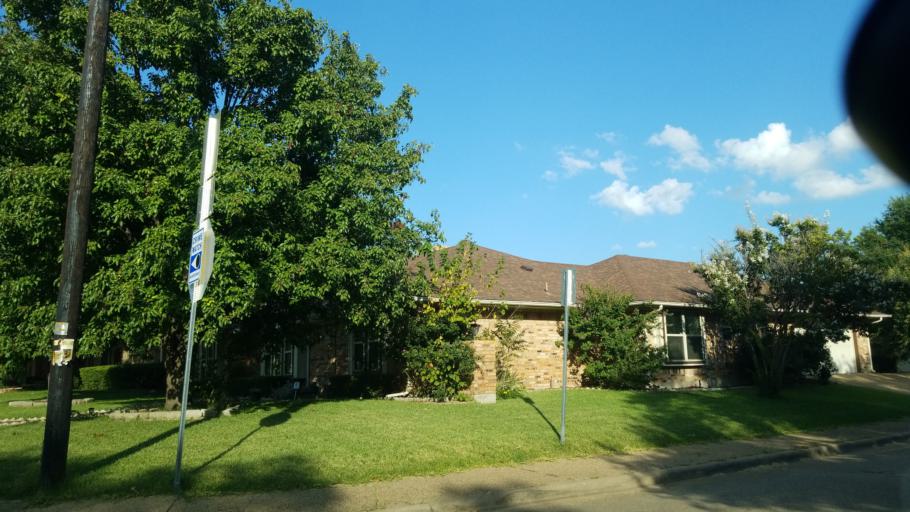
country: US
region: Texas
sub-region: Dallas County
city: Highland Park
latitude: 32.7839
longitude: -96.7070
